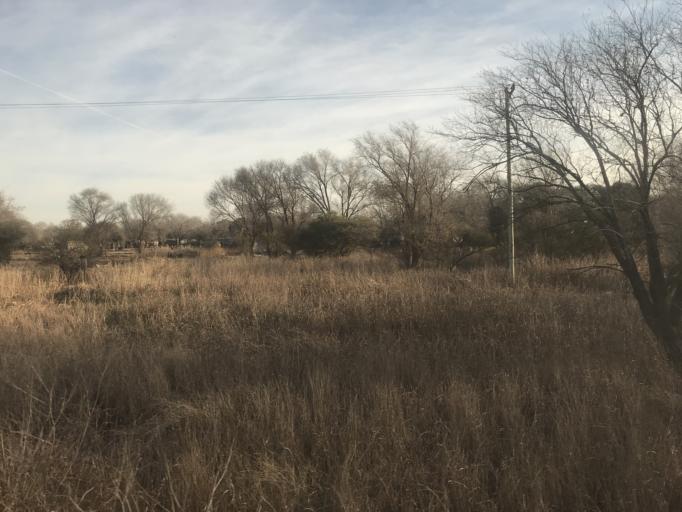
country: AR
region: Cordoba
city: Malvinas Argentinas
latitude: -31.4650
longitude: -64.1031
